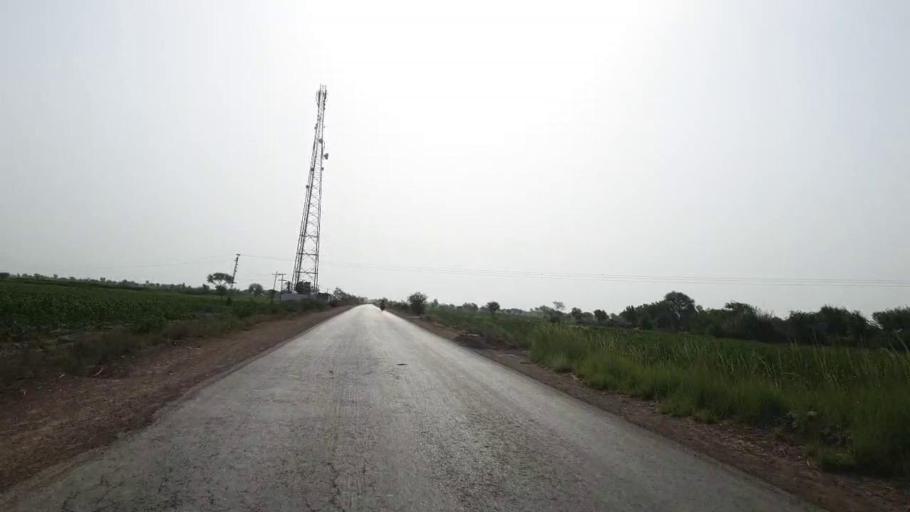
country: PK
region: Sindh
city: Jam Sahib
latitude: 26.2692
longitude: 68.5252
